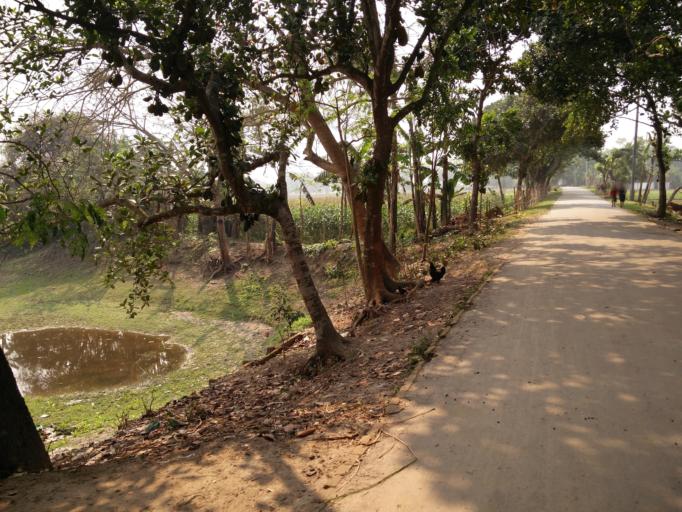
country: BD
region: Dhaka
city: Muktagacha
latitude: 24.9066
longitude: 90.1861
